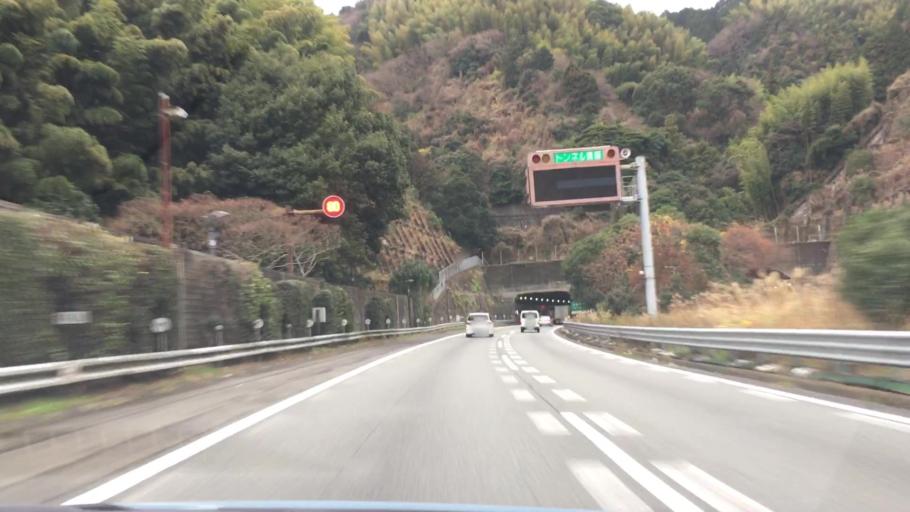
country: JP
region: Shizuoka
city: Shizuoka-shi
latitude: 35.0544
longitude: 138.5164
